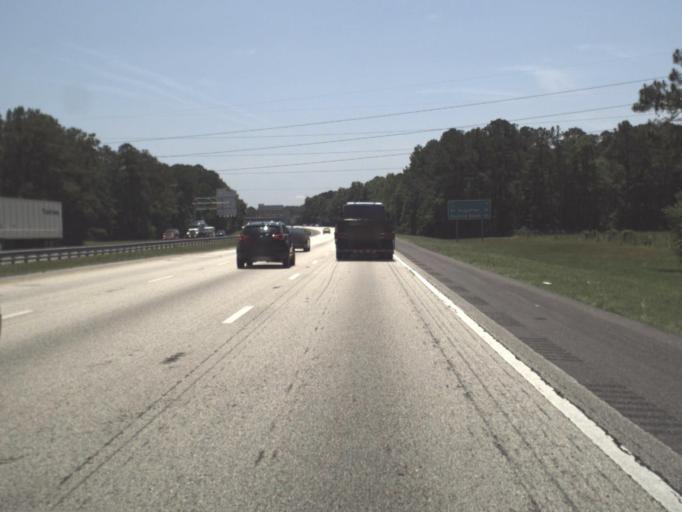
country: US
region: Florida
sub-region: Saint Johns County
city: Fruit Cove
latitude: 30.1491
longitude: -81.5460
